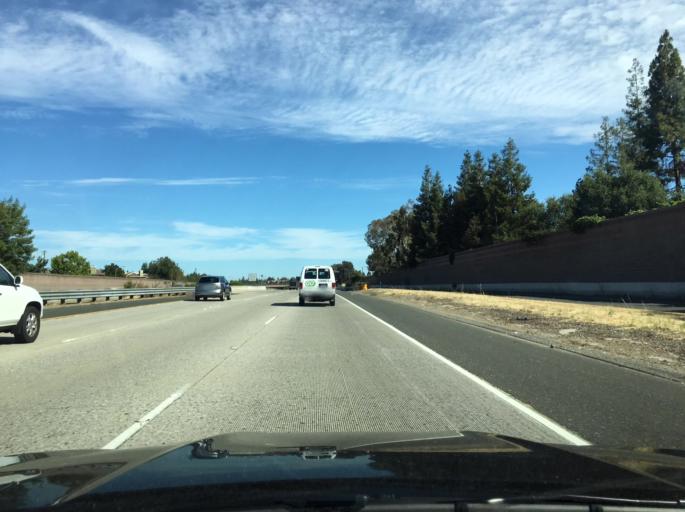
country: US
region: California
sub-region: Santa Clara County
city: Cupertino
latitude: 37.2969
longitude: -122.0281
